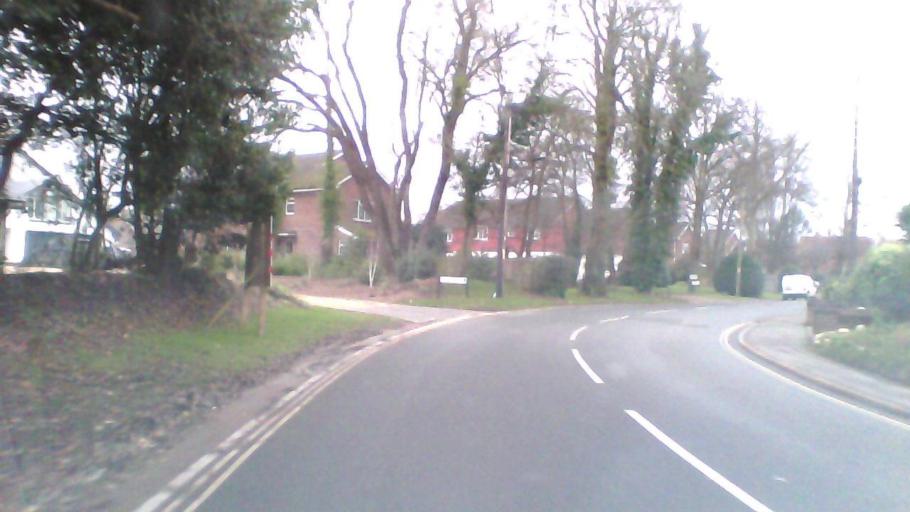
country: GB
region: England
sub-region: Isle of Wight
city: Bembridge
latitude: 50.6879
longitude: -1.0854
